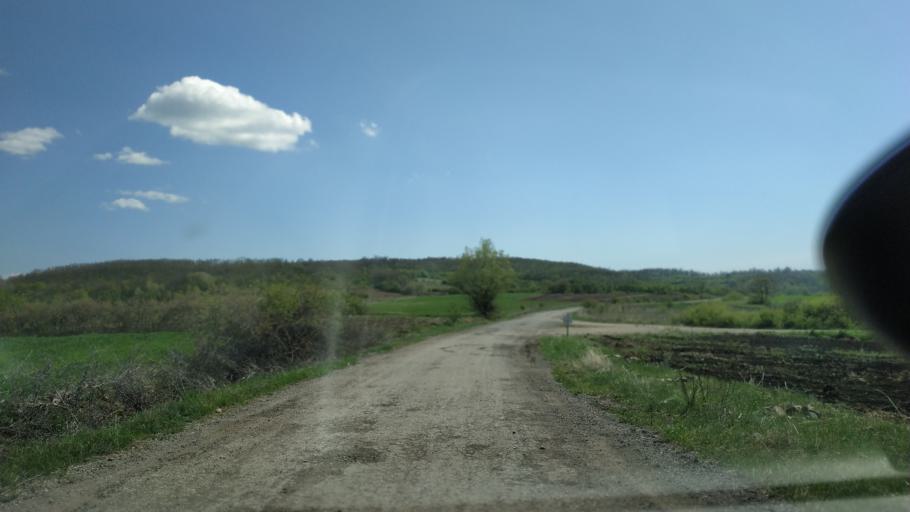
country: RS
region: Central Serbia
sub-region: Zajecarski Okrug
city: Soko Banja
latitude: 43.5157
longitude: 21.9057
